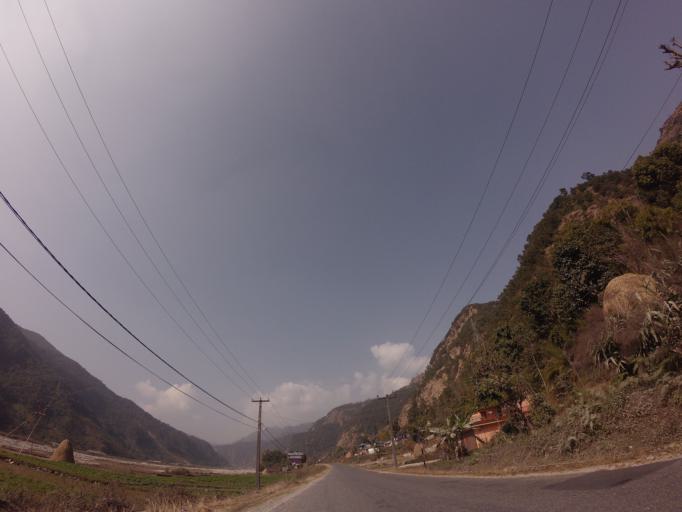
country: NP
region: Western Region
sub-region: Gandaki Zone
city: Pokhara
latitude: 28.2878
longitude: 83.8975
